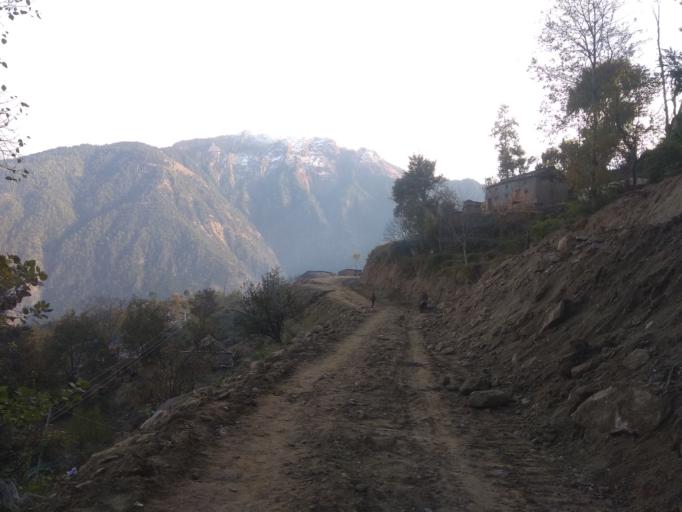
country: NP
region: Mid Western
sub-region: Bheri Zone
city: Dailekh
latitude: 29.2511
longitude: 81.6602
